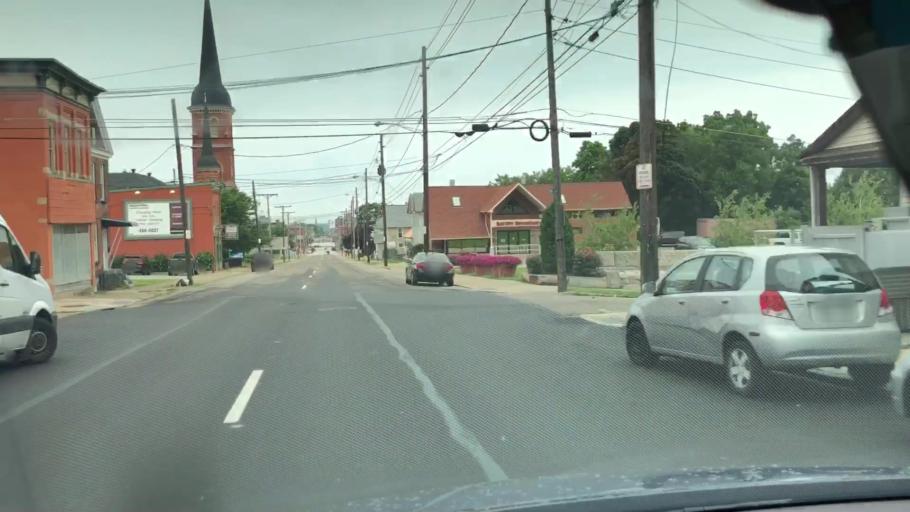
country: US
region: Pennsylvania
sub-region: Erie County
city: Erie
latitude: 42.1129
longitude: -80.0759
